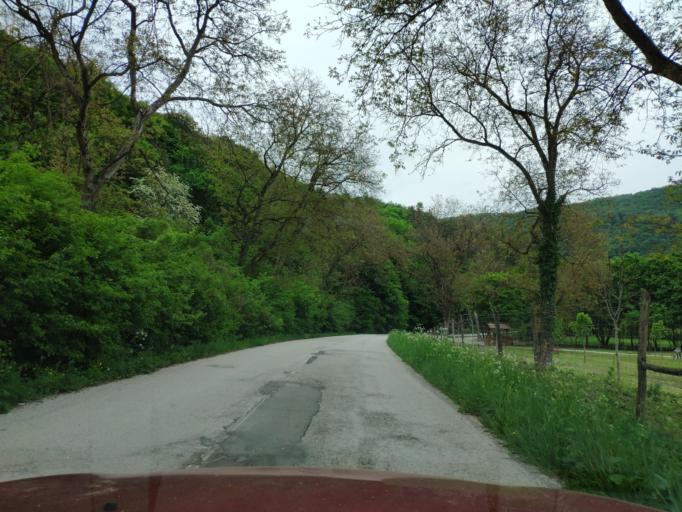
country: SK
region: Kosicky
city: Roznava
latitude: 48.5685
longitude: 20.4669
